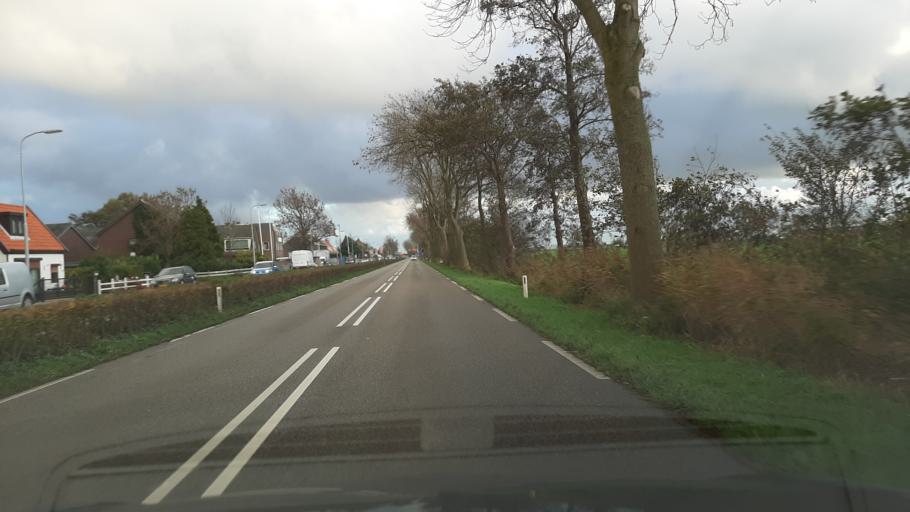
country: NL
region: North Holland
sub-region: Gemeente Haarlemmermeer
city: Hoofddorp
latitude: 52.3620
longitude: 4.7222
